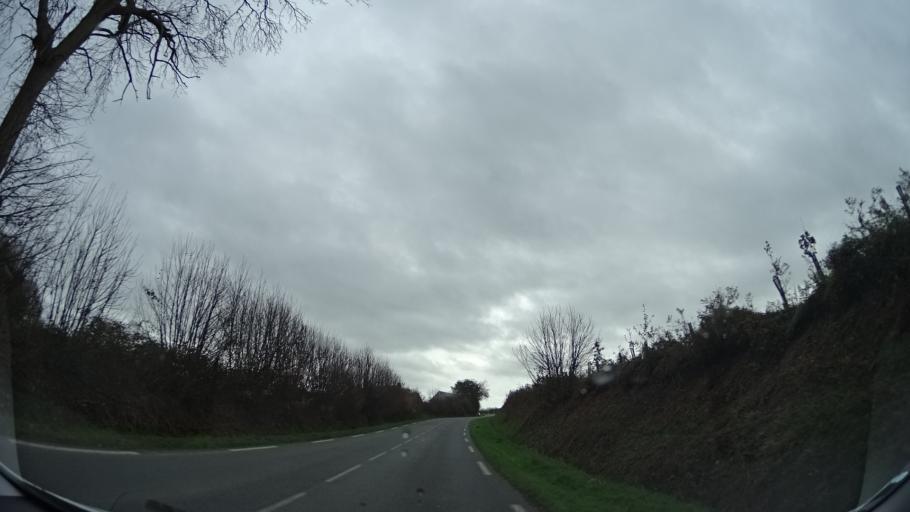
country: FR
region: Brittany
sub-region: Departement des Cotes-d'Armor
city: Les Champs-Geraux
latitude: 48.4167
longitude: -1.9997
